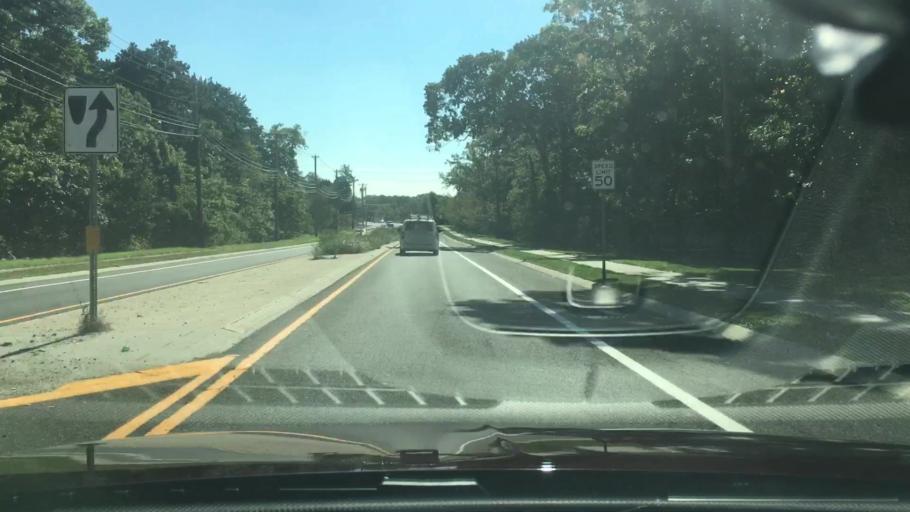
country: US
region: New York
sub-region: Suffolk County
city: Port Jefferson Station
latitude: 40.9076
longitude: -73.0279
